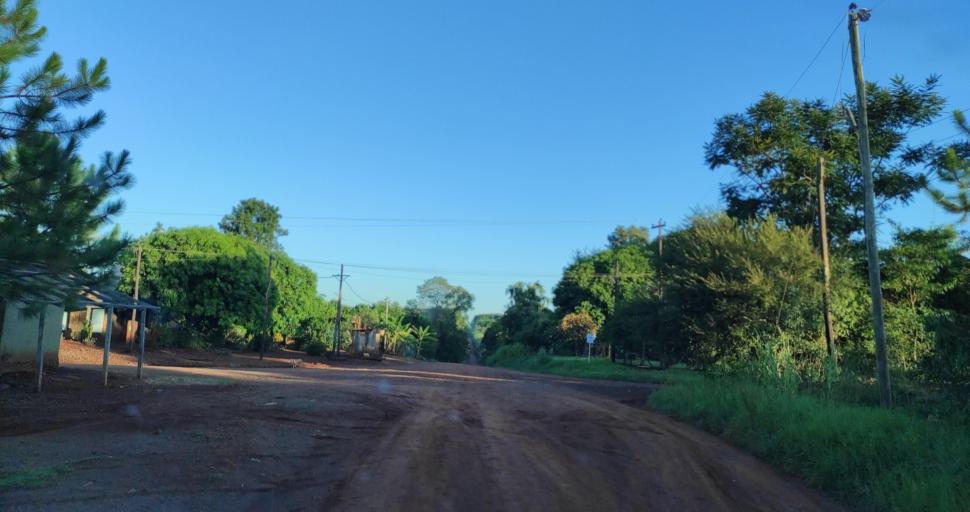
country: AR
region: Misiones
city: Gobernador Roca
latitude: -27.2243
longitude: -55.4318
